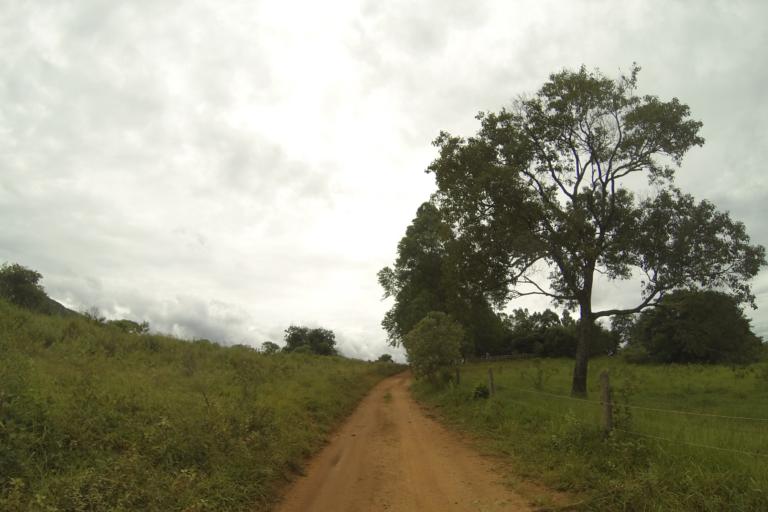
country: BR
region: Minas Gerais
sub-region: Ibia
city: Ibia
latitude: -19.7505
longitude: -46.5259
